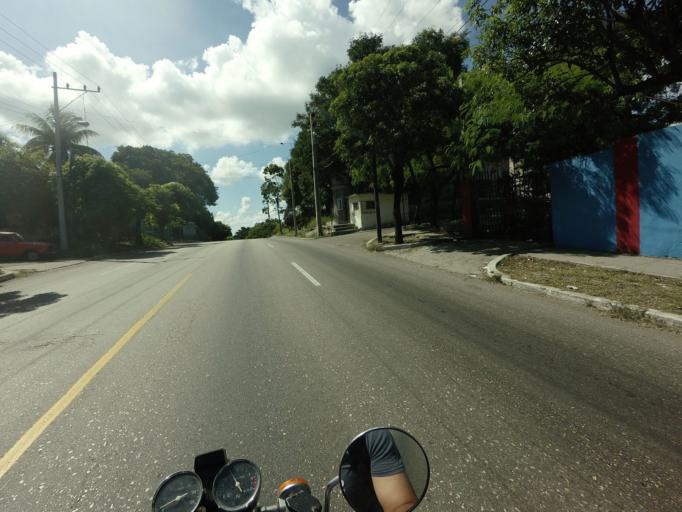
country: TM
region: Balkan
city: Gumdag
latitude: 38.8434
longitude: 54.1793
